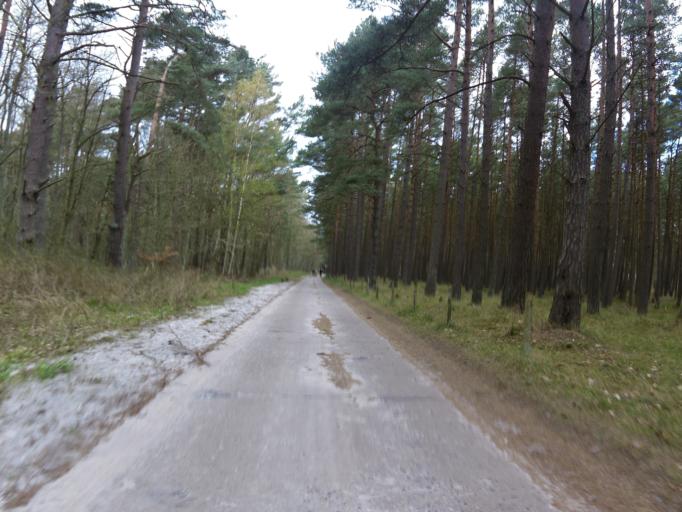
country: DE
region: Mecklenburg-Vorpommern
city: Ostseebad Prerow
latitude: 54.4594
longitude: 12.5351
